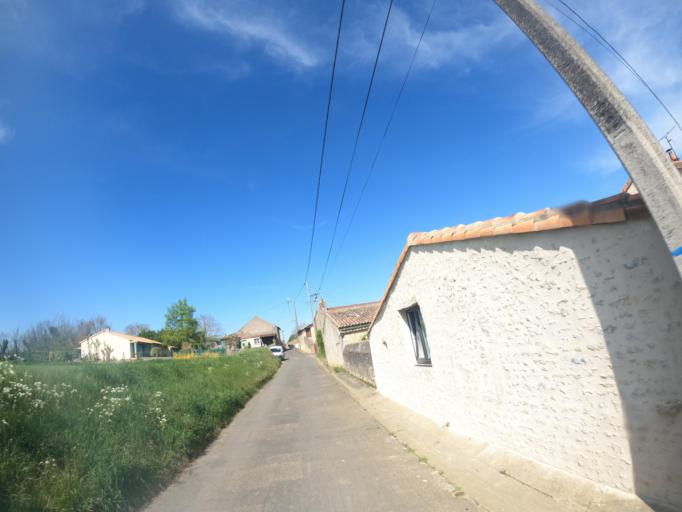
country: FR
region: Poitou-Charentes
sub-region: Departement des Deux-Sevres
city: Saint-Varent
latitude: 46.9084
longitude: -0.2149
